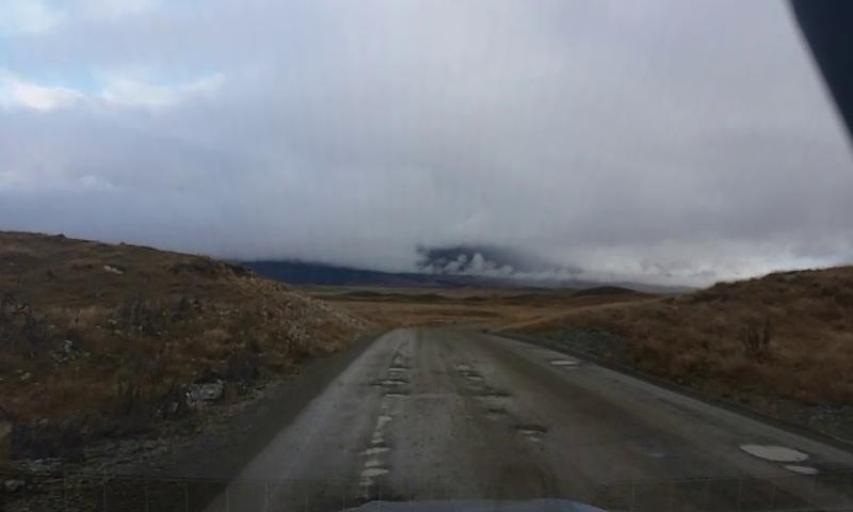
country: NZ
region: Canterbury
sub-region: Ashburton District
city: Methven
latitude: -43.6162
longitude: 171.1335
